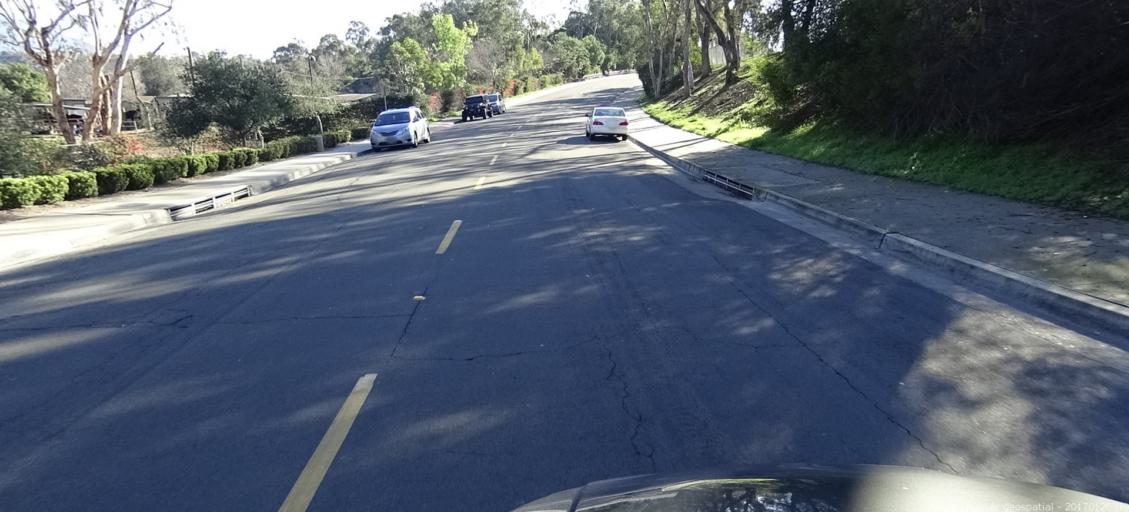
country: US
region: California
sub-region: Orange County
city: Lake Forest
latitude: 33.6474
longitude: -117.6925
